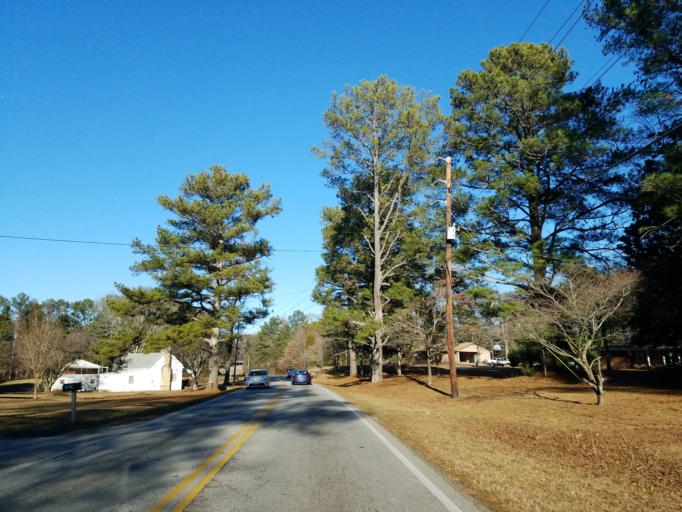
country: US
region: Georgia
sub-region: Douglas County
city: Lithia Springs
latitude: 33.7438
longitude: -84.6641
